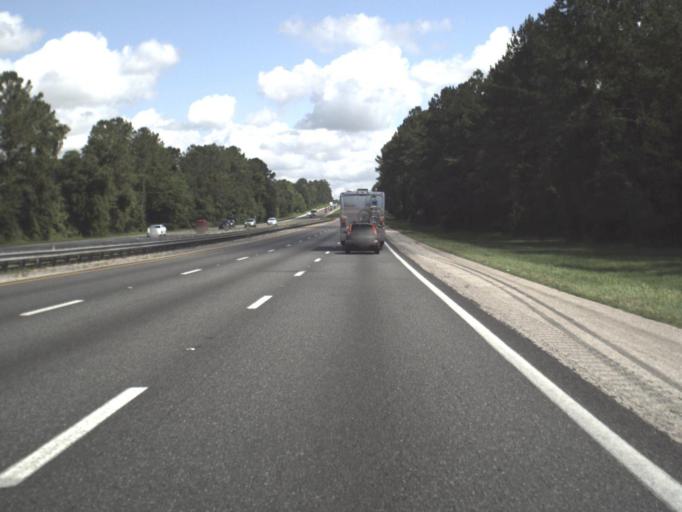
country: US
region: Florida
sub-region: Alachua County
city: Alachua
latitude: 29.7247
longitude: -82.4703
